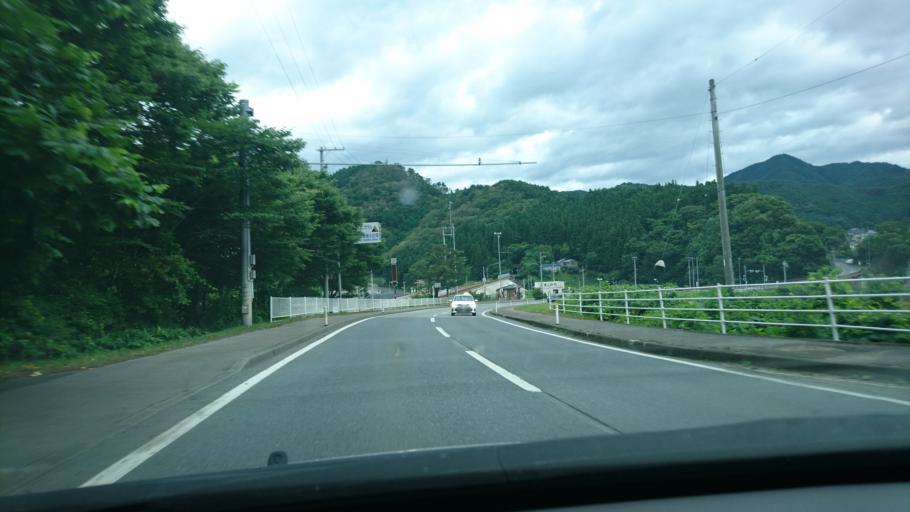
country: JP
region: Iwate
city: Kamaishi
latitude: 39.2007
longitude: 141.8612
